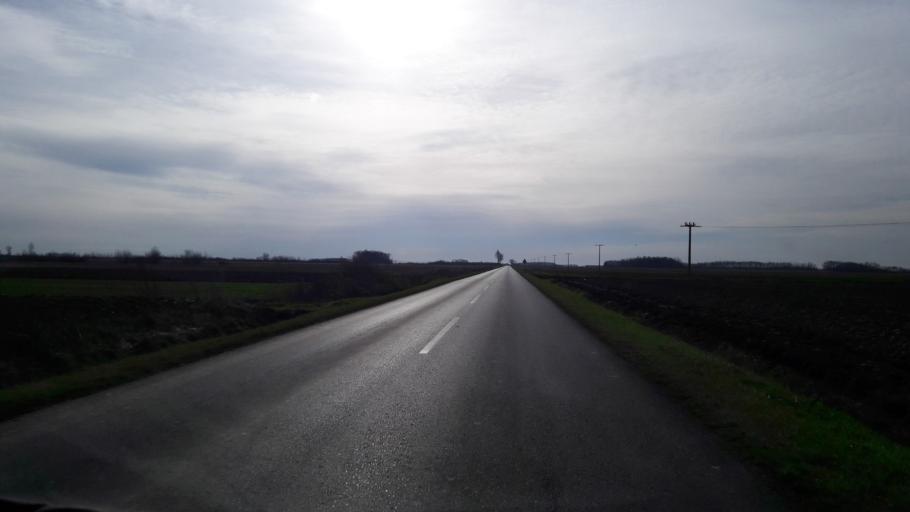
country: HR
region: Osjecko-Baranjska
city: Semeljci
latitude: 45.3371
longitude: 18.5575
